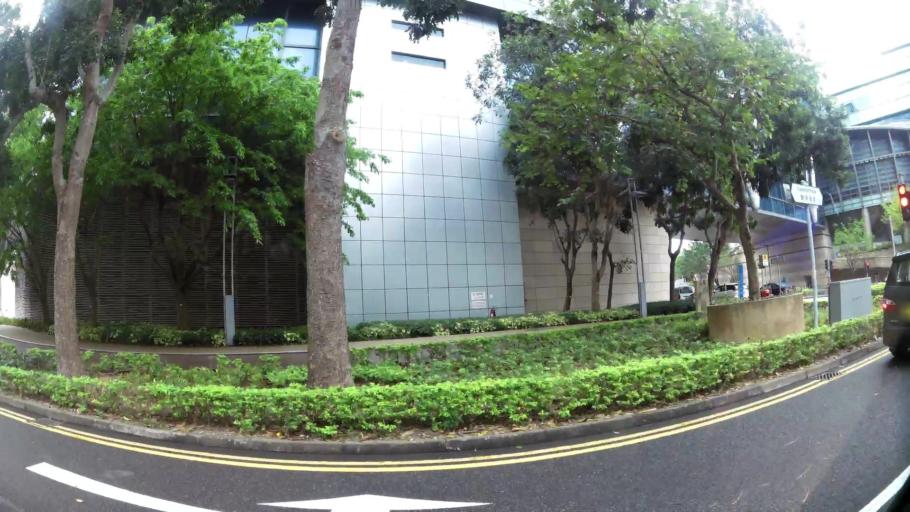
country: HK
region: Central and Western
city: Central
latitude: 22.2608
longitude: 114.1312
